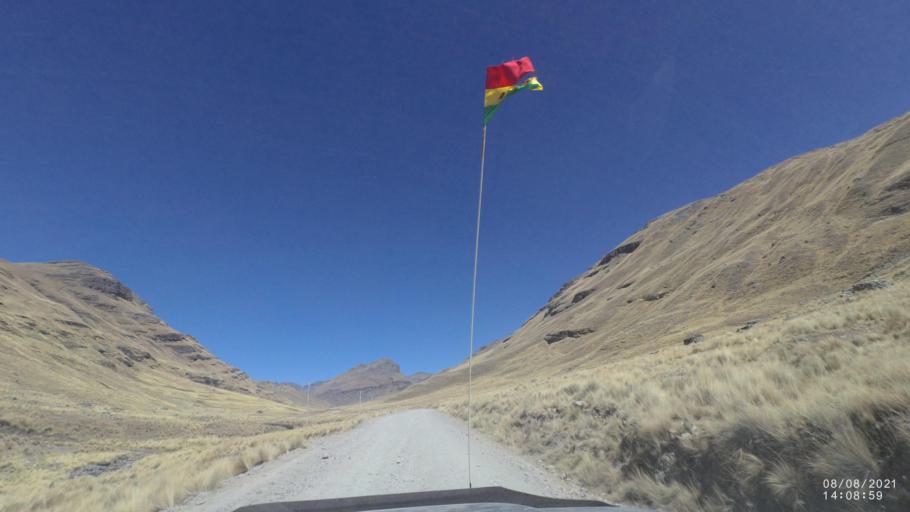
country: BO
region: Cochabamba
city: Sipe Sipe
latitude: -17.1422
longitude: -66.4394
